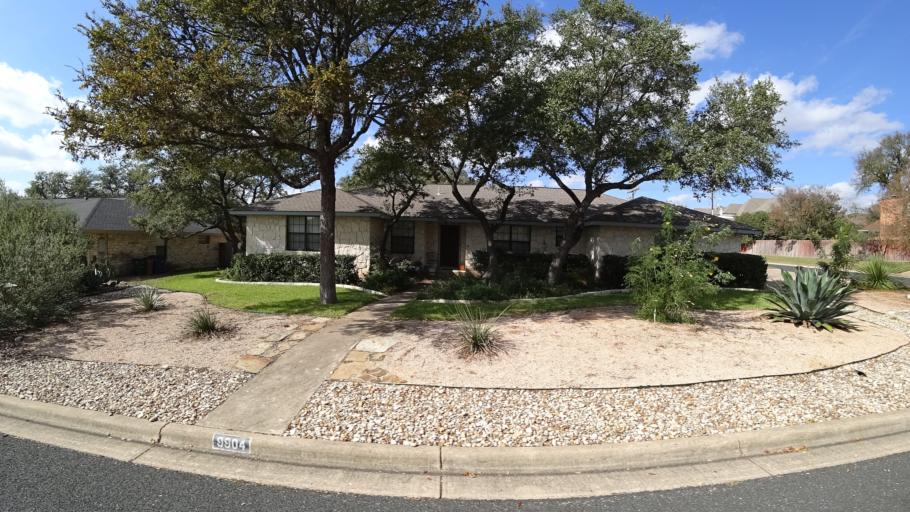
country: US
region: Texas
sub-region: Williamson County
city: Anderson Mill
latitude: 30.4242
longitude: -97.8053
